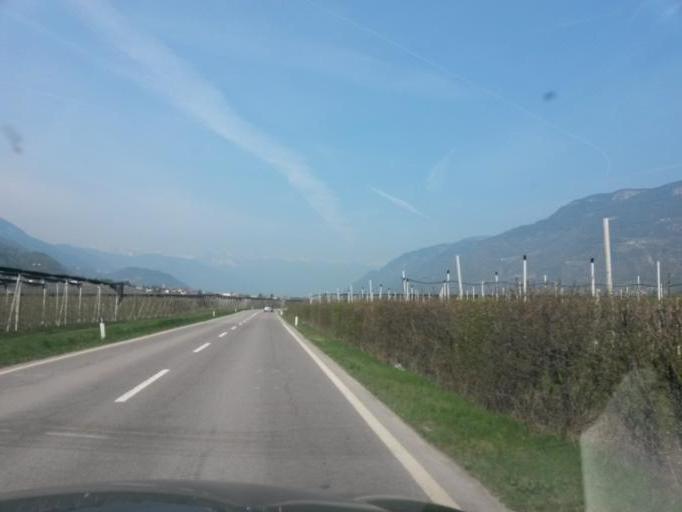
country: IT
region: Trentino-Alto Adige
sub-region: Bolzano
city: Andriano
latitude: 46.5059
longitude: 11.2472
